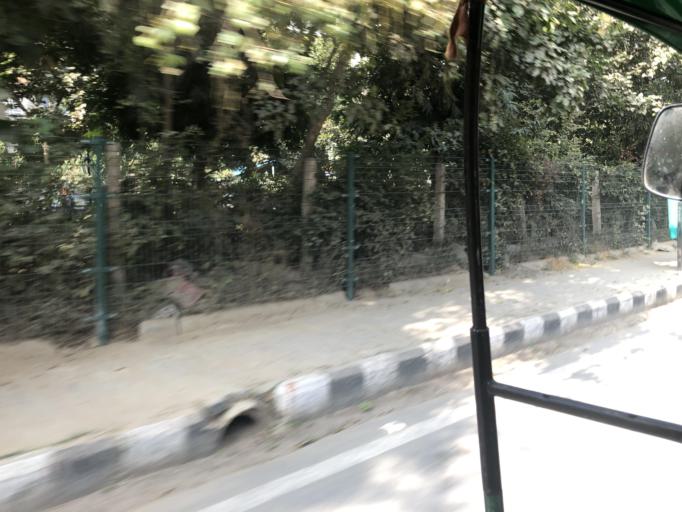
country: IN
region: Haryana
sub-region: Gurgaon
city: Gurgaon
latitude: 28.4335
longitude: 77.0907
